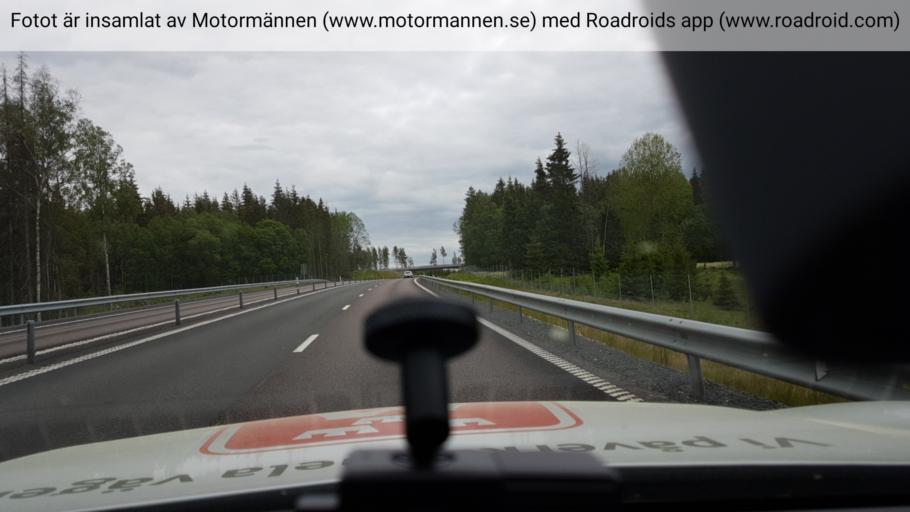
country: SE
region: Joenkoeping
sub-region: Mullsjo Kommun
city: Mullsjoe
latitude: 57.8957
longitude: 13.8755
